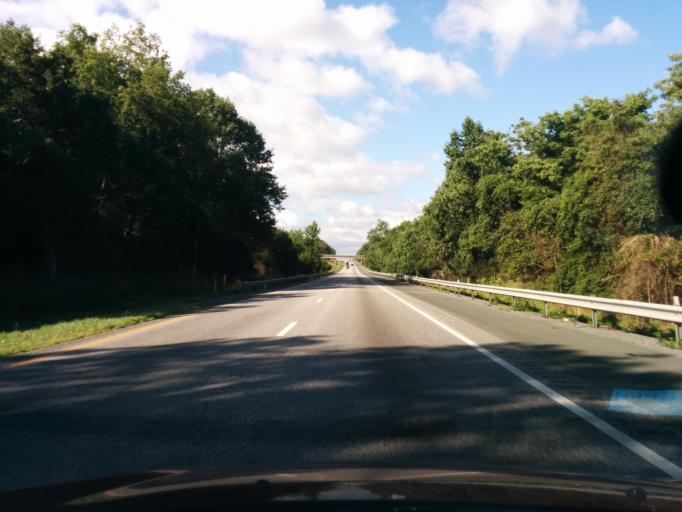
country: US
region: Virginia
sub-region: City of Lexington
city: Lexington
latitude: 37.7439
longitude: -79.4203
